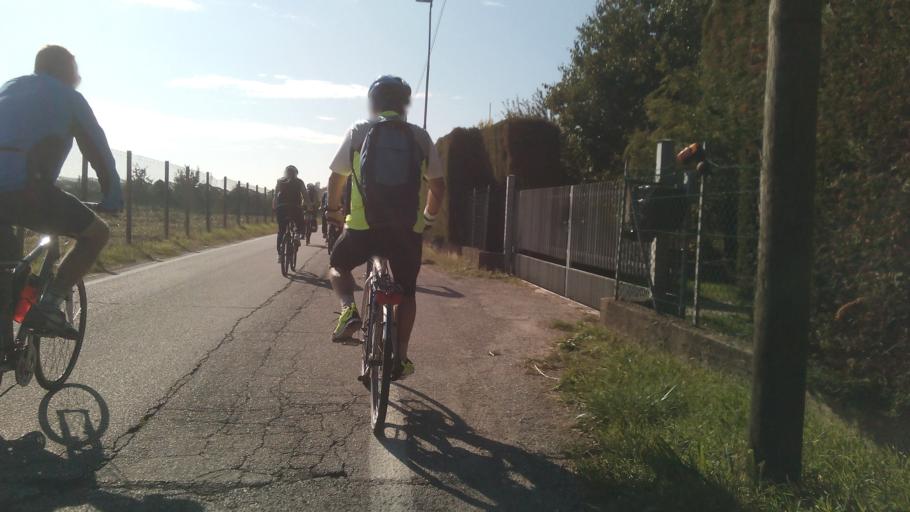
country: IT
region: Veneto
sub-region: Provincia di Verona
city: Beccacivetta-Azzano
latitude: 45.3531
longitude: 10.9712
